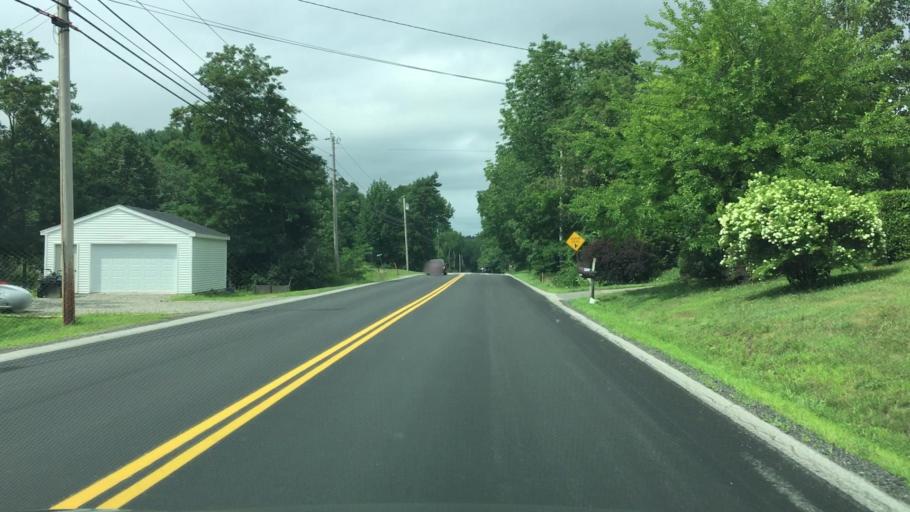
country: US
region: Maine
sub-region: Waldo County
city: Winterport
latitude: 44.6081
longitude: -68.8206
